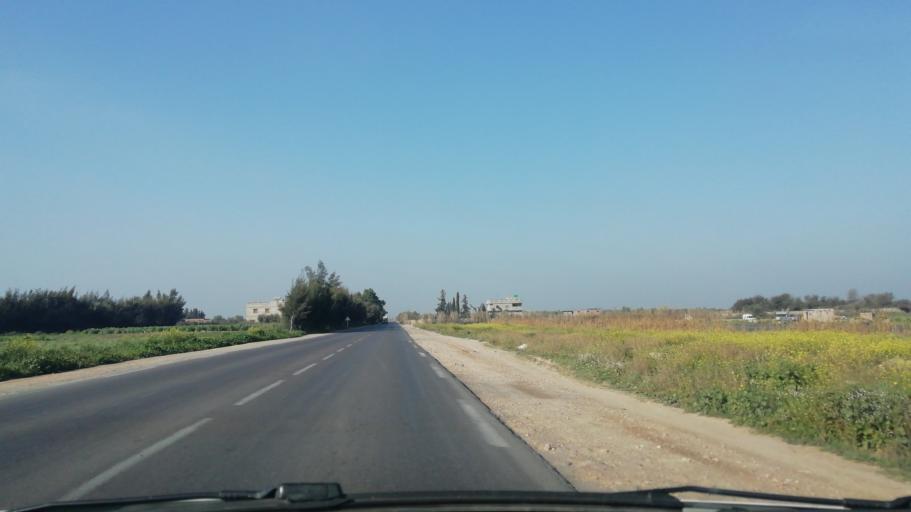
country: DZ
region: Mostaganem
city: Mostaganem
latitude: 35.7471
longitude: 0.1585
